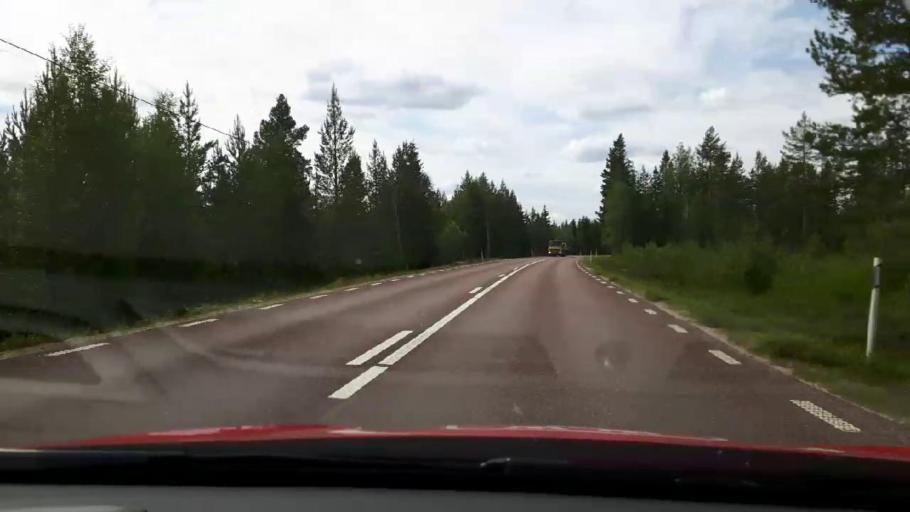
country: SE
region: Jaemtland
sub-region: Harjedalens Kommun
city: Sveg
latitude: 62.0561
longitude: 14.5627
